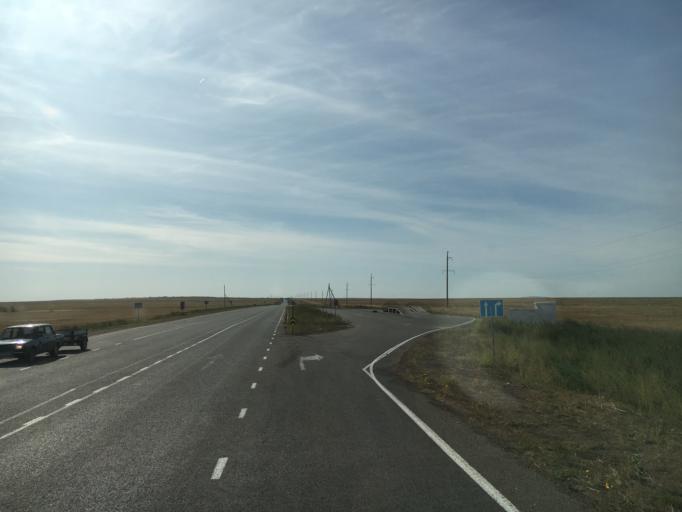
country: KZ
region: Batys Qazaqstan
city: Peremetnoe
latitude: 51.1171
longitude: 50.6250
